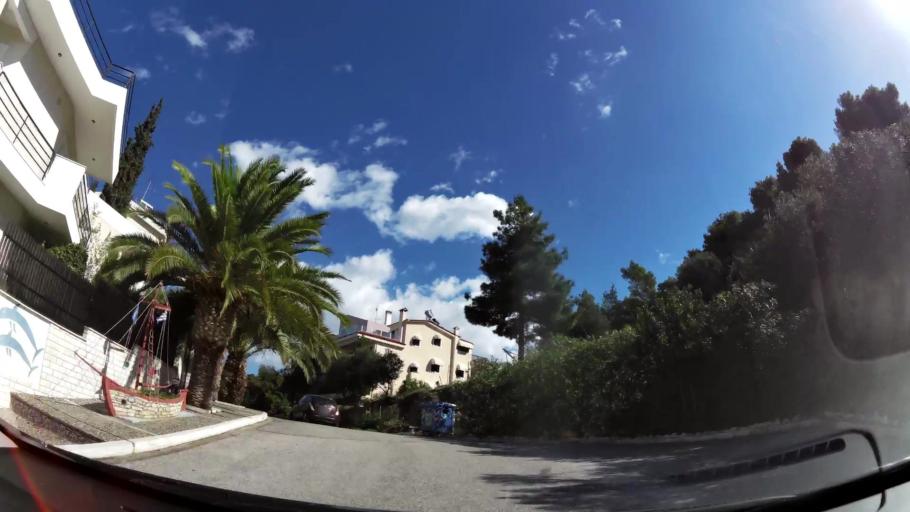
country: GR
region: Attica
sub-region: Nomarchia Anatolikis Attikis
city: Voula
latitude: 37.8300
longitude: 23.7807
